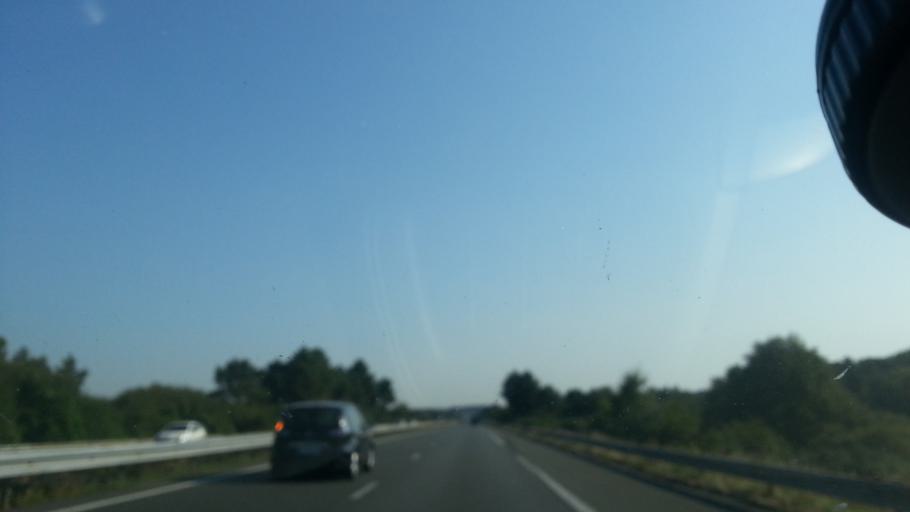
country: FR
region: Poitou-Charentes
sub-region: Departement de la Vienne
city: Antran
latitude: 46.9128
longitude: 0.5272
